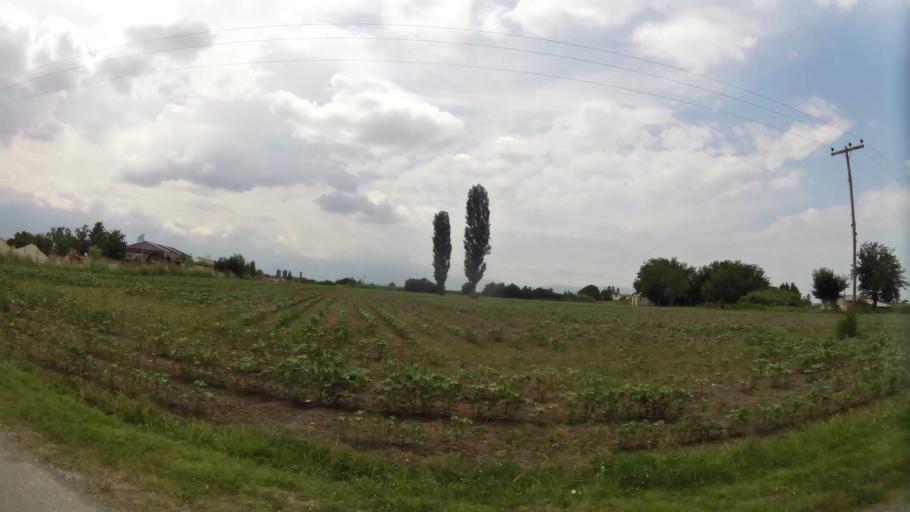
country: GR
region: Central Macedonia
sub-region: Nomos Pierias
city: Kallithea
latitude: 40.2748
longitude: 22.5703
